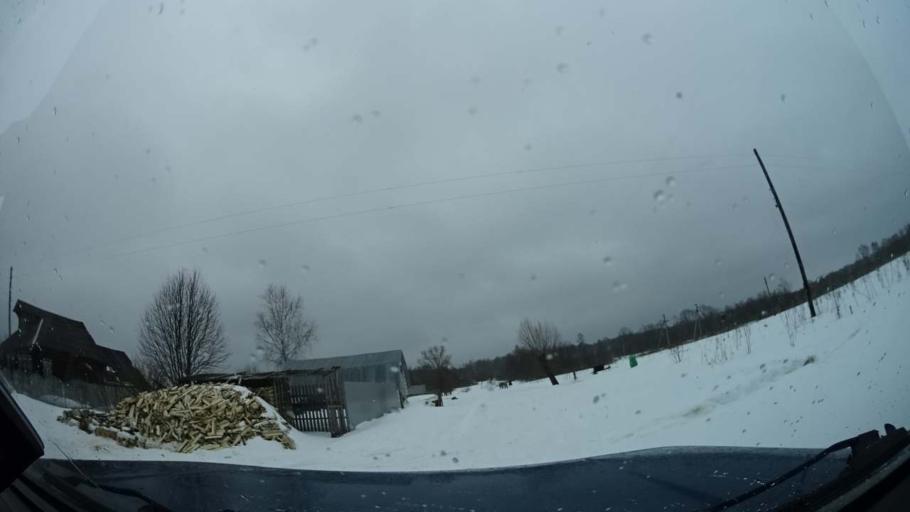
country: RU
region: Tverskaya
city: Gorodnya
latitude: 56.8311
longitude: 36.4016
